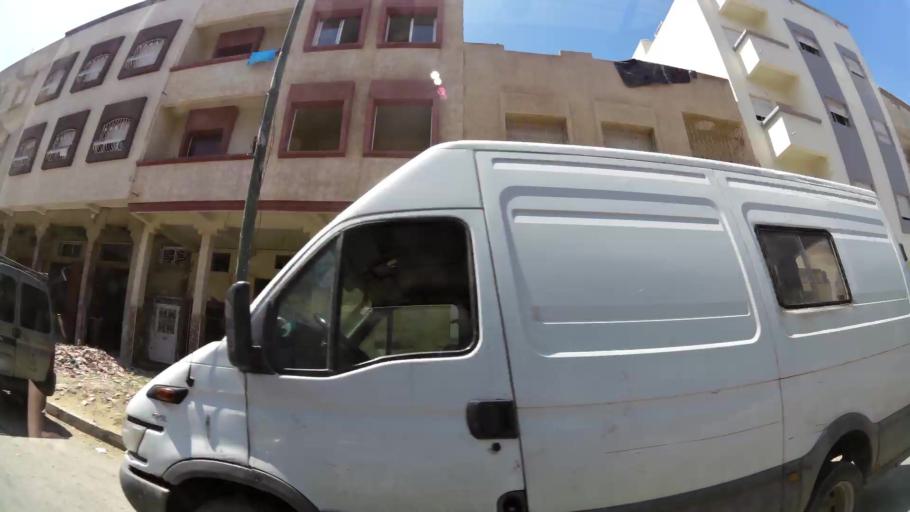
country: MA
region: Gharb-Chrarda-Beni Hssen
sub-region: Kenitra Province
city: Kenitra
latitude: 34.2452
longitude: -6.5401
